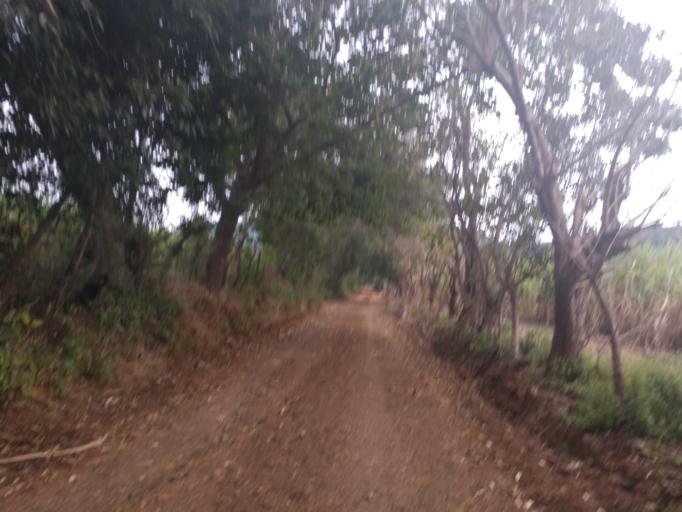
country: MX
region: Nayarit
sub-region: Tepic
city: La Corregidora
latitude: 21.4708
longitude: -104.7923
